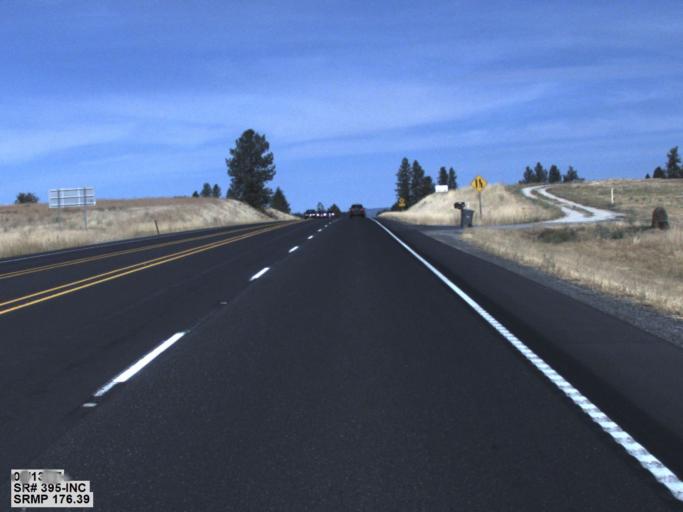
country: US
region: Washington
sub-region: Spokane County
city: Deer Park
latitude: 47.9045
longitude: -117.4406
